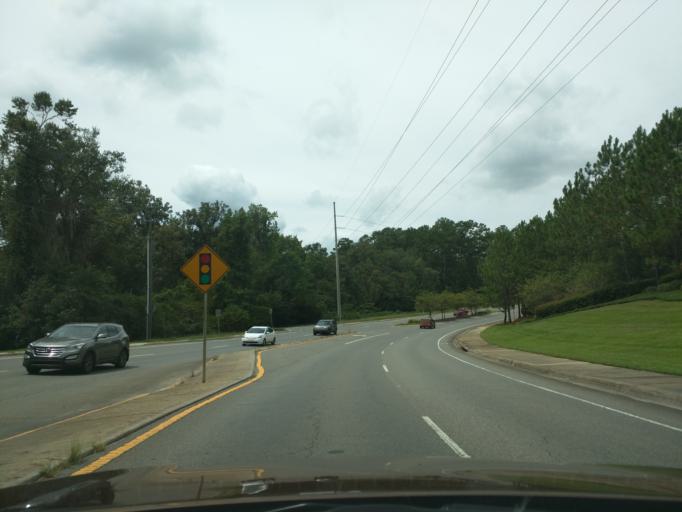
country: US
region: Florida
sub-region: Leon County
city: Tallahassee
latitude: 30.5603
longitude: -84.2142
